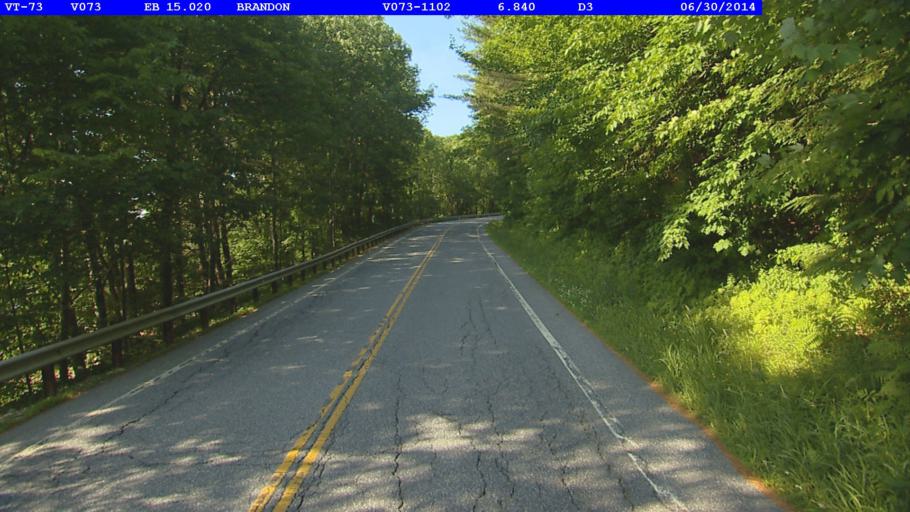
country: US
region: Vermont
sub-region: Rutland County
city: Brandon
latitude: 43.8372
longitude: -73.0408
